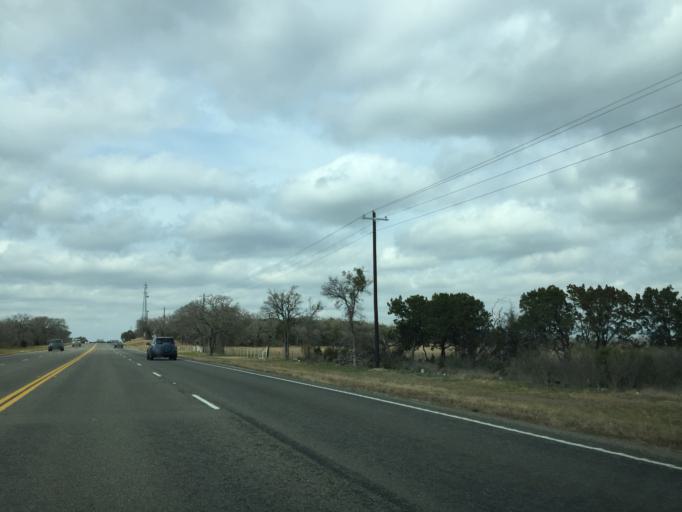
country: US
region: Texas
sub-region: Burnet County
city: Marble Falls
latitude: 30.4772
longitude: -98.1896
